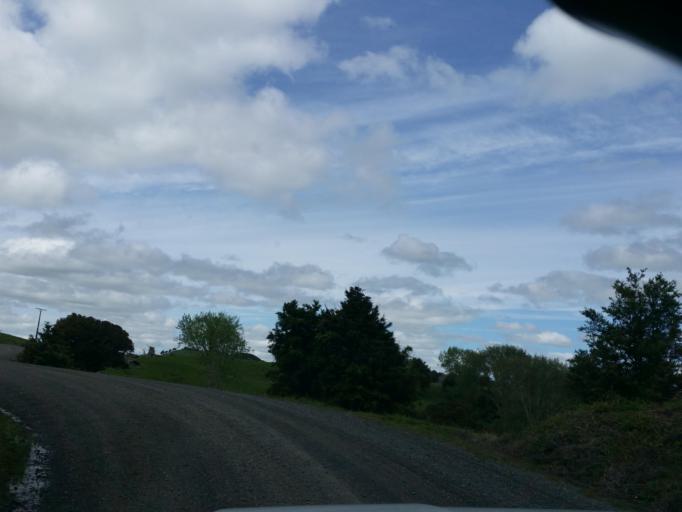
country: NZ
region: Northland
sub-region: Whangarei
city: Maungatapere
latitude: -35.8995
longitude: 174.0992
